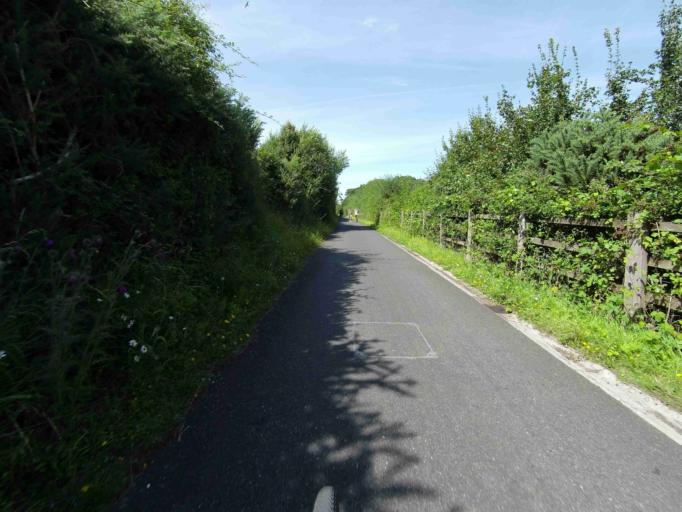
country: GB
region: England
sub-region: Devon
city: Topsham
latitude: 50.6775
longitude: -3.4502
